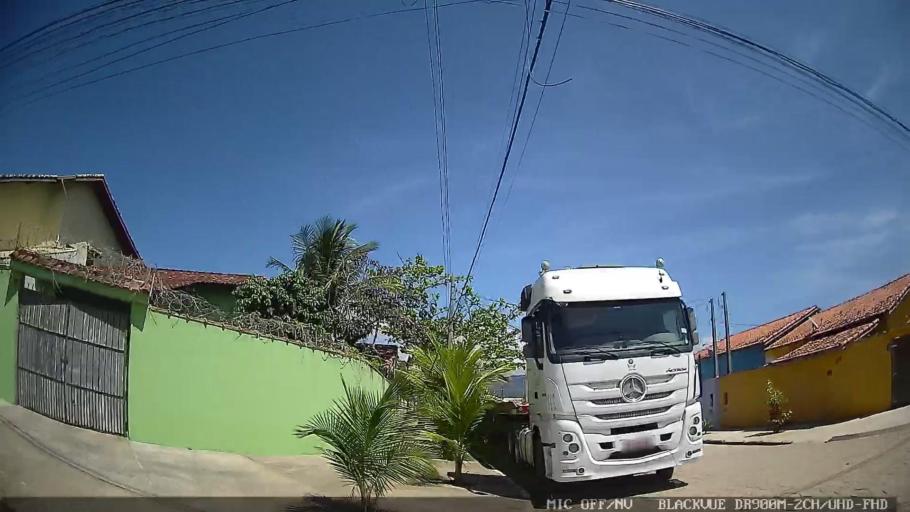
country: BR
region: Sao Paulo
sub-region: Peruibe
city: Peruibe
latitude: -24.3002
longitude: -46.9910
